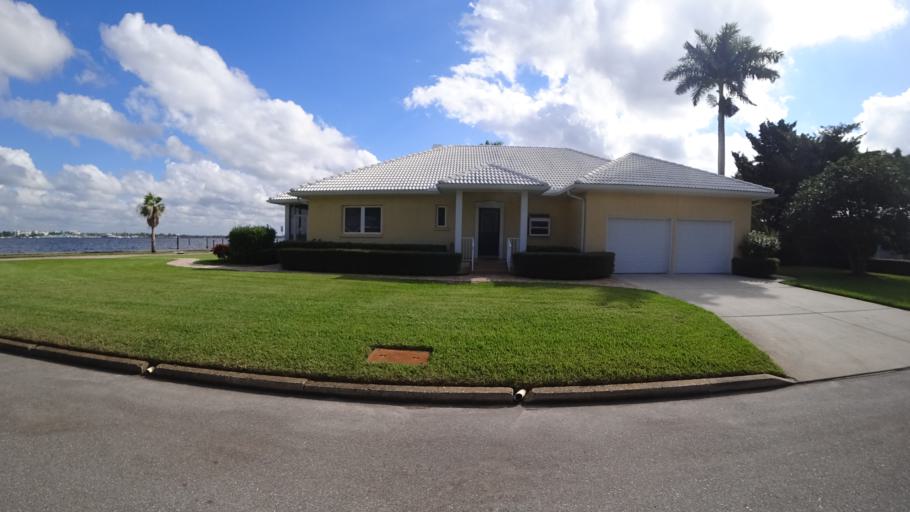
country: US
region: Florida
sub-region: Manatee County
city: Bradenton
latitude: 27.4998
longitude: -82.5851
